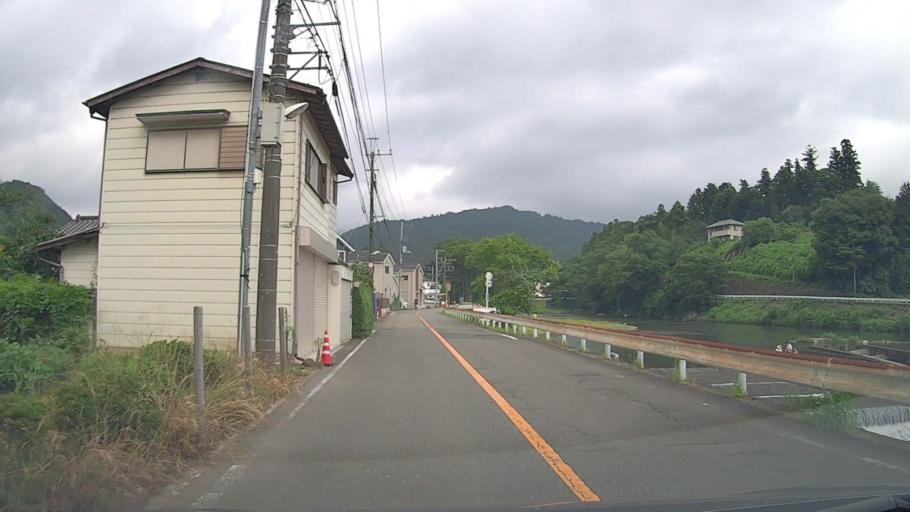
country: JP
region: Tokyo
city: Itsukaichi
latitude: 35.7229
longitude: 139.2238
